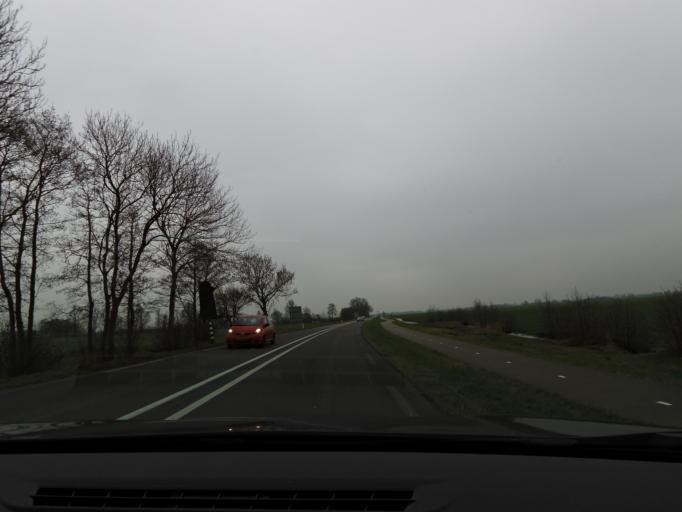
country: NL
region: Utrecht
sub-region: Gemeente De Ronde Venen
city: Mijdrecht
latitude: 52.1594
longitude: 4.9109
